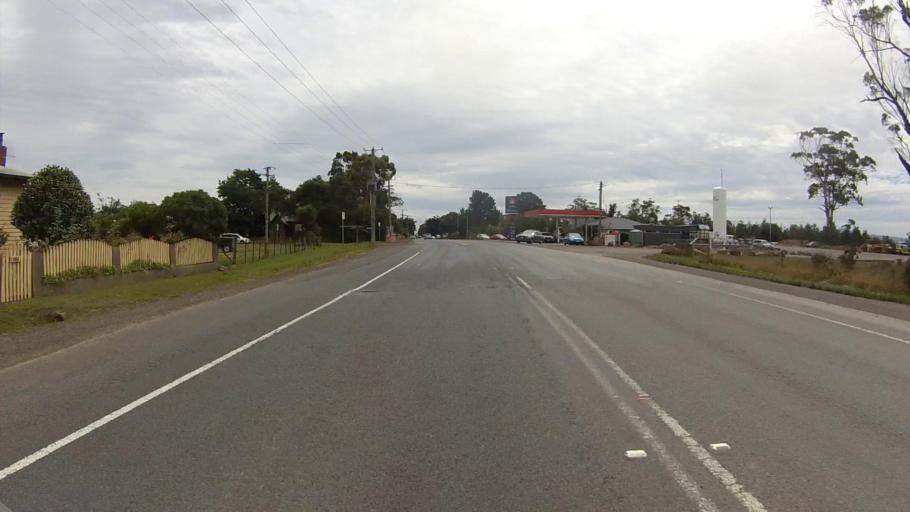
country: AU
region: Tasmania
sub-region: Northern Midlands
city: Evandale
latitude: -41.7607
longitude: 147.3519
